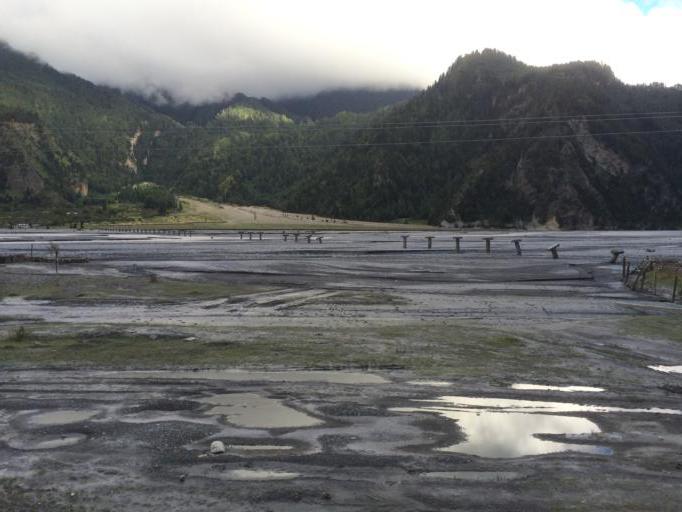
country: NP
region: Western Region
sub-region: Dhawalagiri Zone
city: Jomsom
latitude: 28.6949
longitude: 83.6226
